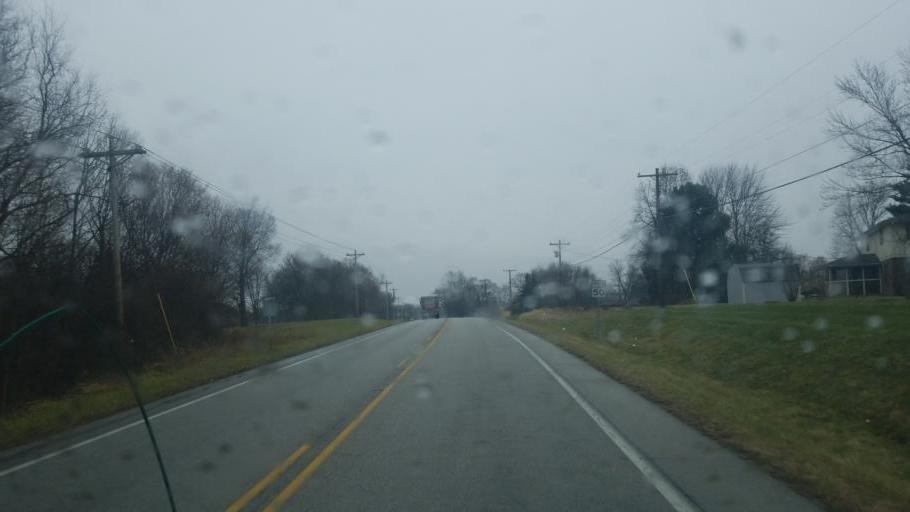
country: US
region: Indiana
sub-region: Shelby County
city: Shelbyville
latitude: 39.5696
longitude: -85.7767
